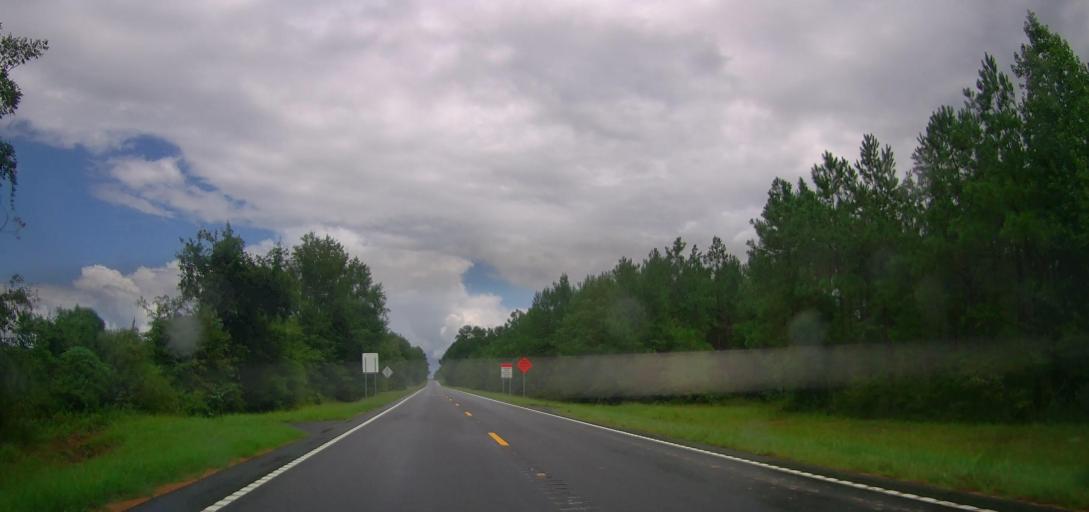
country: US
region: Georgia
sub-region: Wilcox County
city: Rochelle
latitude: 32.1038
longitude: -83.5814
